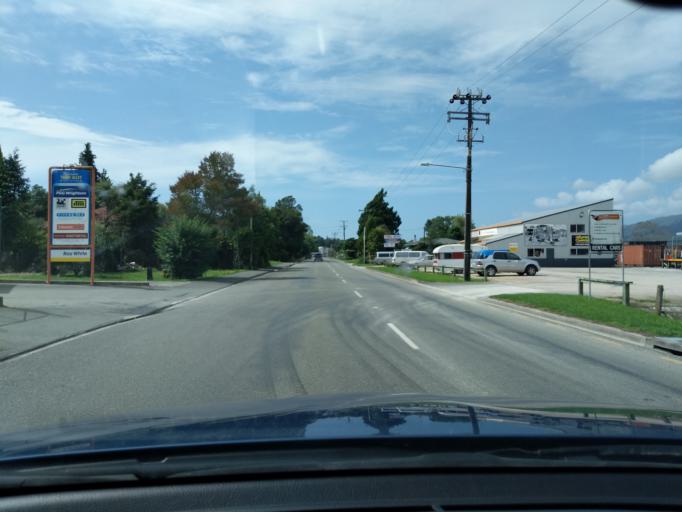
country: NZ
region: Tasman
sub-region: Tasman District
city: Takaka
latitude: -40.8590
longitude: 172.8087
